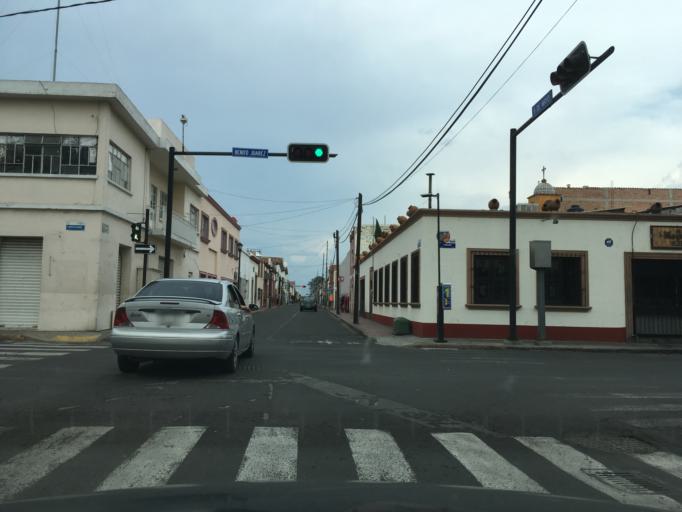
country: MX
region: Guanajuato
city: Celaya
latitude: 20.5248
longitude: -100.8153
